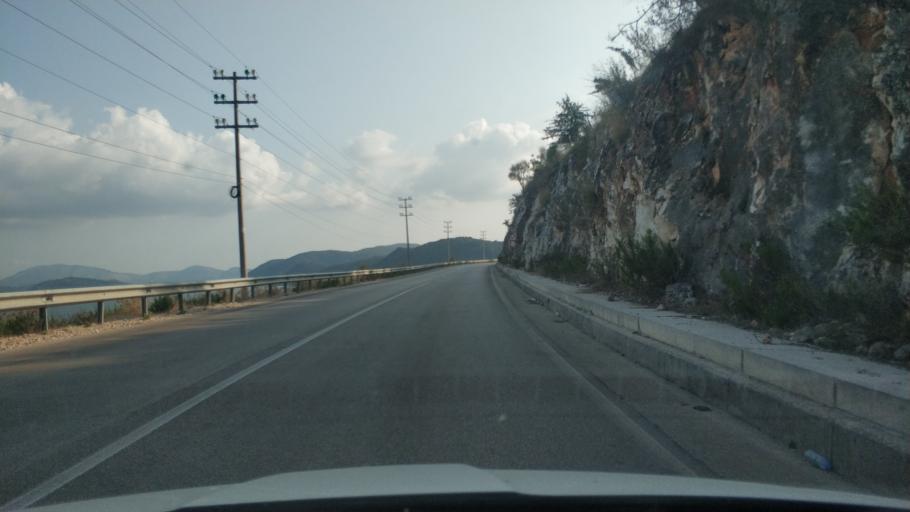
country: AL
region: Vlore
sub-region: Rrethi i Sarandes
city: Sarande
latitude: 39.7997
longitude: 20.0120
